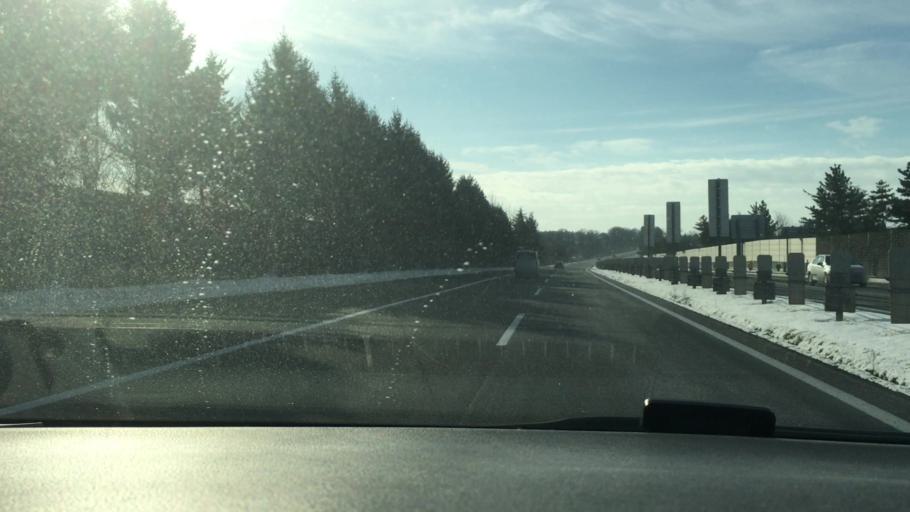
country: JP
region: Iwate
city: Hanamaki
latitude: 39.3796
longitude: 141.0926
